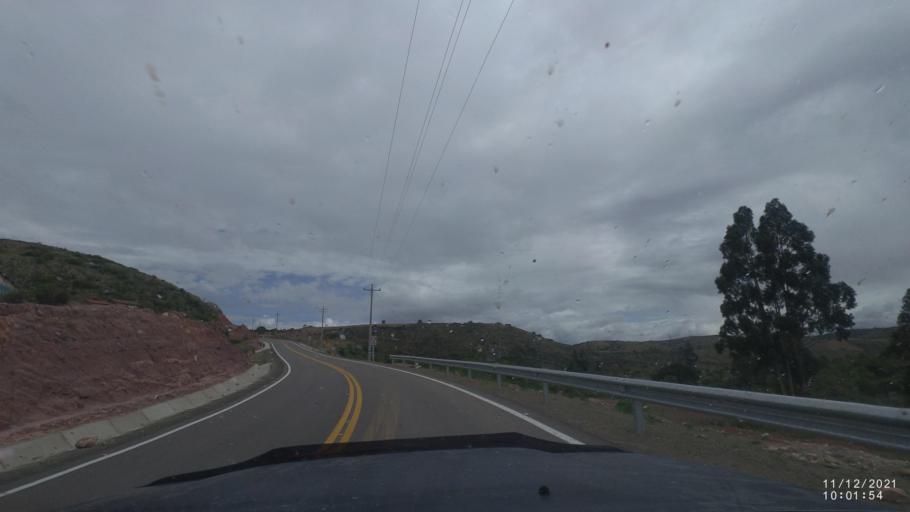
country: BO
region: Cochabamba
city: Cliza
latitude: -17.7246
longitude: -65.9305
